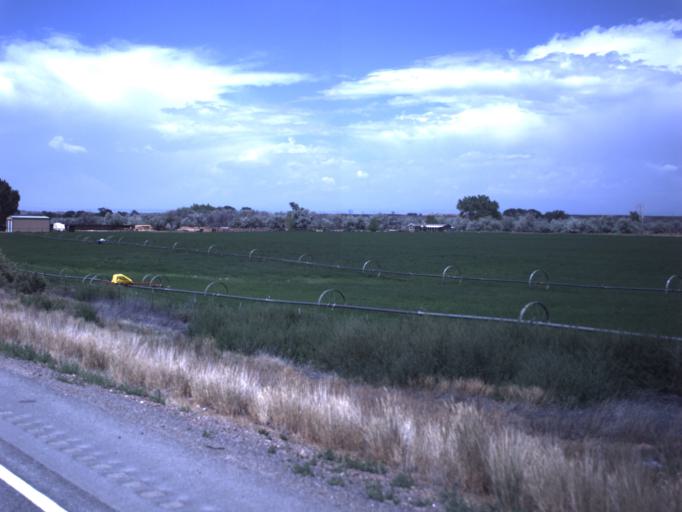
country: US
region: Utah
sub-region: Duchesne County
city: Roosevelt
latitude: 40.3033
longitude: -109.7842
